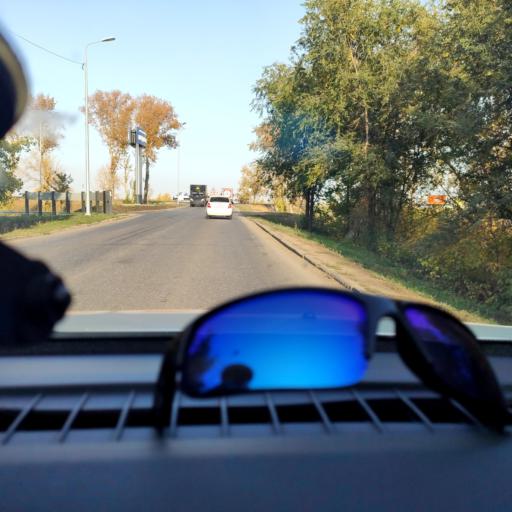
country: RU
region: Samara
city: Samara
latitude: 53.0987
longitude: 50.1414
